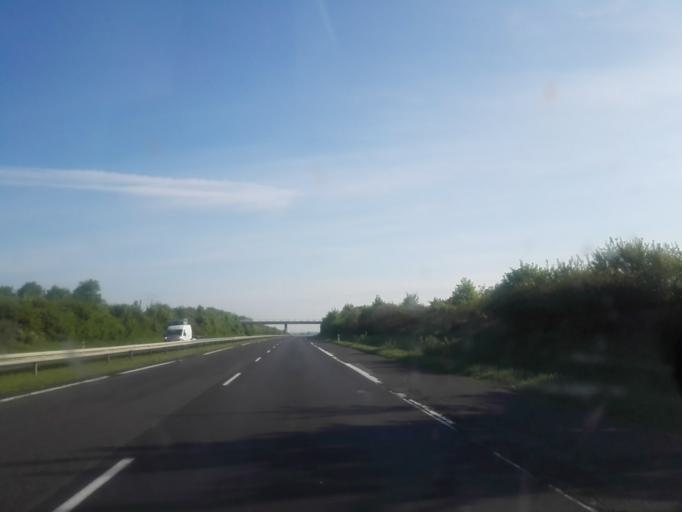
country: PL
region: Lodz Voivodeship
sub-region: Powiat radomszczanski
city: Kamiensk
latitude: 51.1915
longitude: 19.4731
